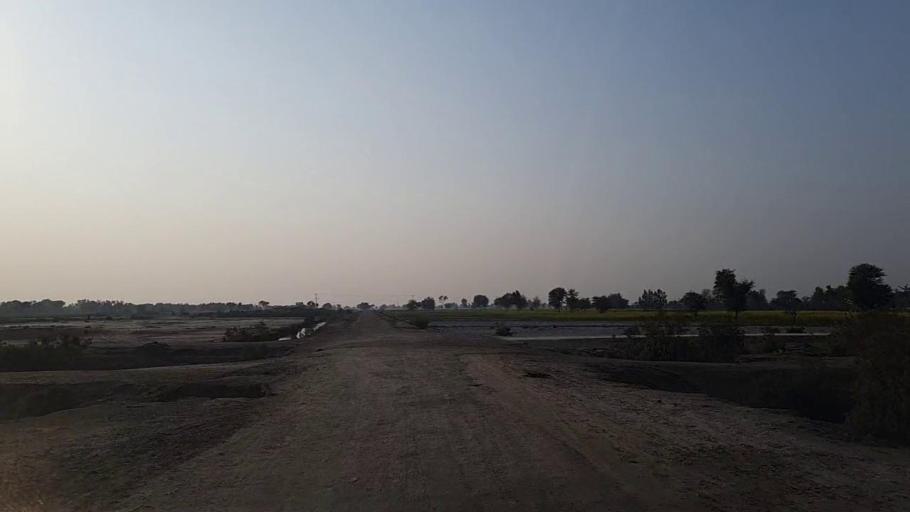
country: PK
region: Sindh
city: Daur
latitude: 26.4071
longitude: 68.3888
